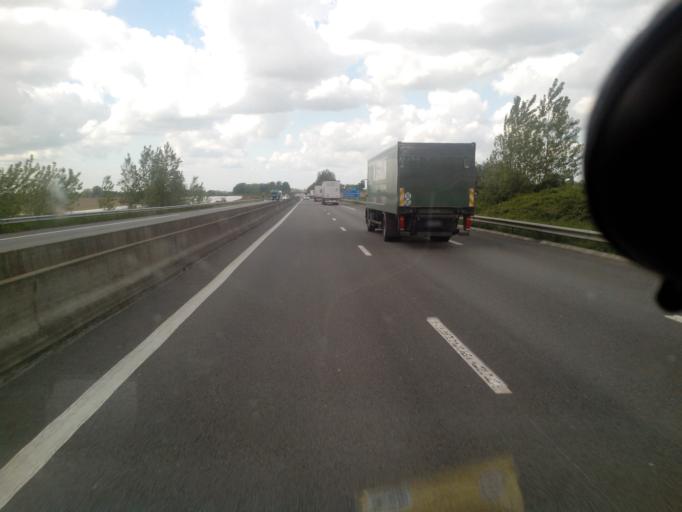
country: FR
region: Nord-Pas-de-Calais
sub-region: Departement du Nord
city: Winnezeele
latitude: 50.8395
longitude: 2.5706
